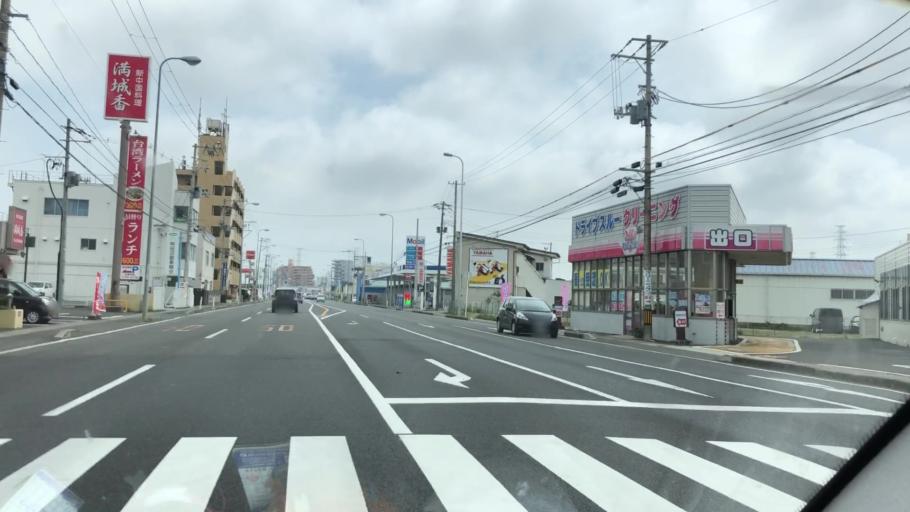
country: JP
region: Miyagi
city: Rifu
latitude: 38.2770
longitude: 140.9779
